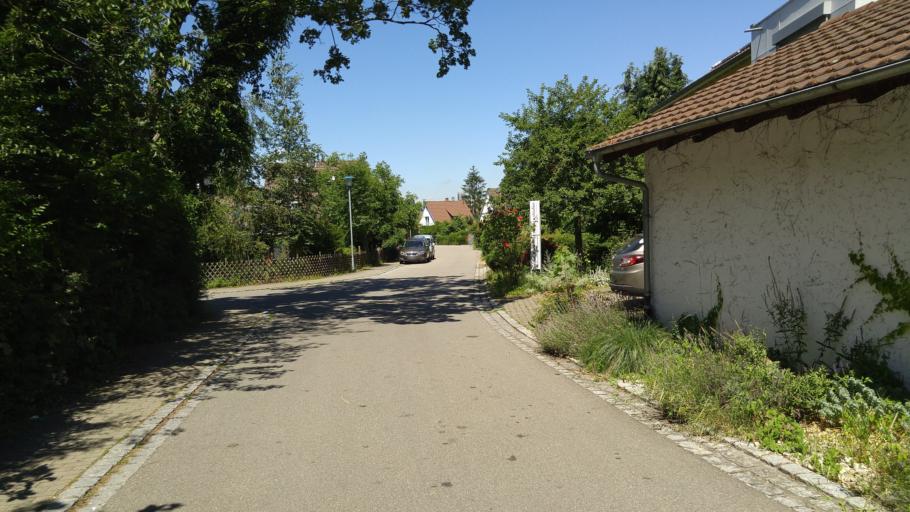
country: DE
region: Baden-Wuerttemberg
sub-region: Freiburg Region
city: Bad Krozingen
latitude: 47.8864
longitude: 7.7262
